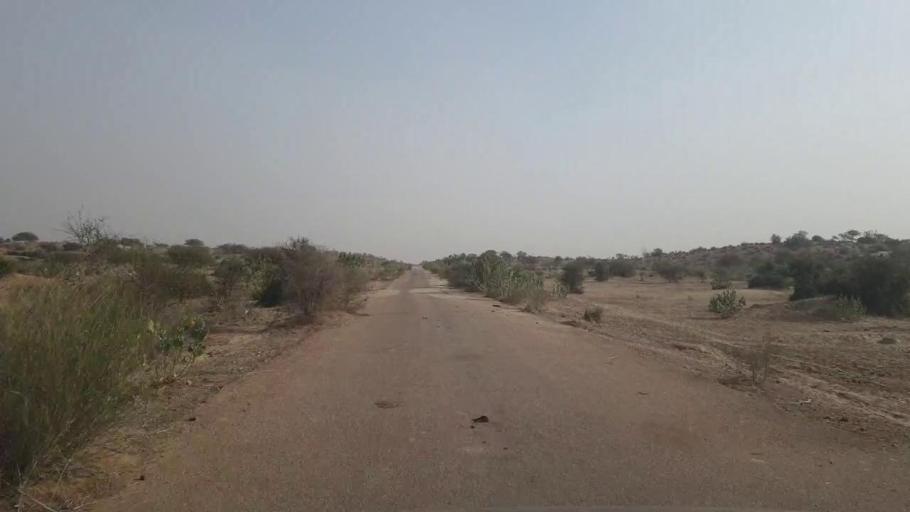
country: PK
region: Sindh
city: Chor
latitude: 25.5122
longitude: 69.9665
